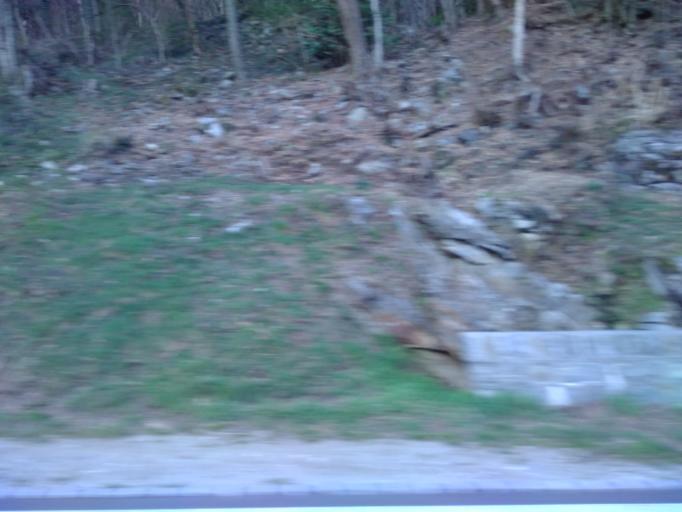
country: CH
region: Ticino
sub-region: Locarno District
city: Verscio
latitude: 46.1933
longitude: 8.7555
